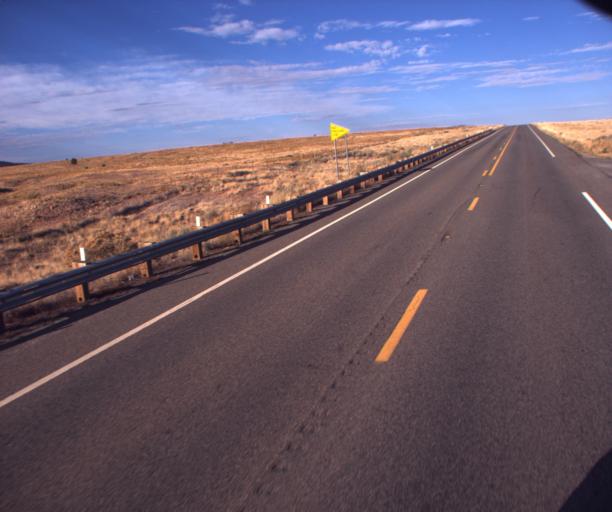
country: US
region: Arizona
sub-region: Apache County
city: Lukachukai
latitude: 36.9270
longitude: -109.1856
